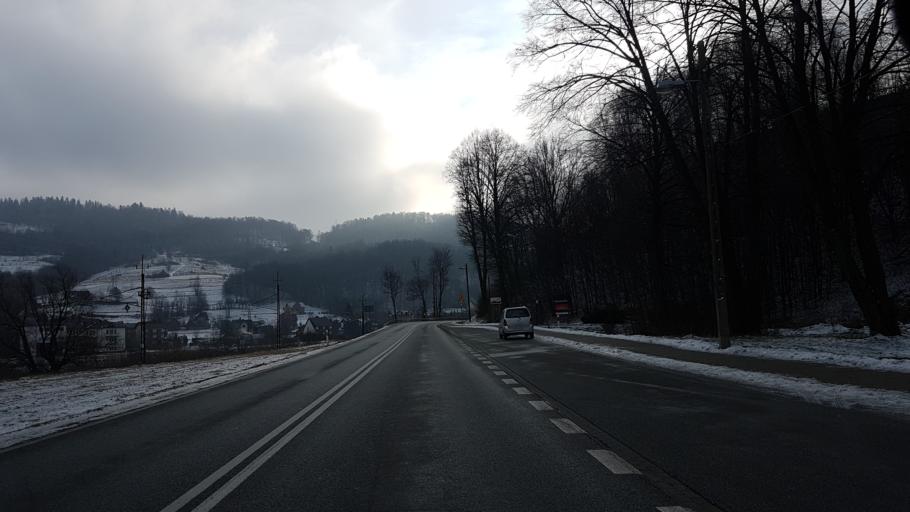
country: PL
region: Lesser Poland Voivodeship
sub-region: Powiat nowosadecki
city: Piwniczna-Zdroj
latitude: 49.4682
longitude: 20.6966
